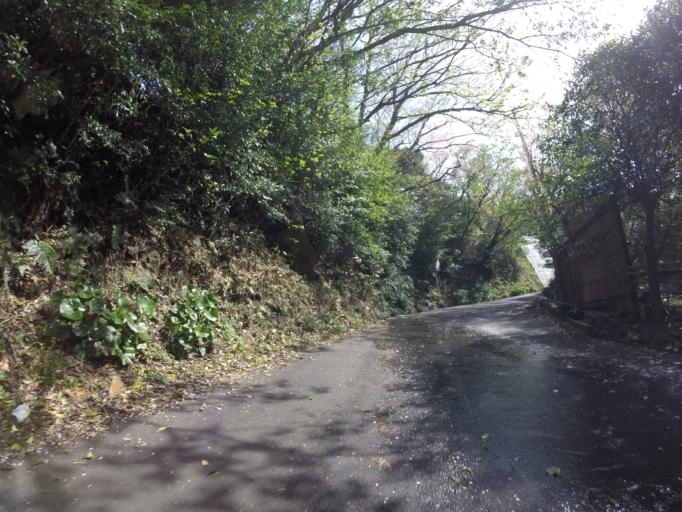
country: JP
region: Shizuoka
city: Heda
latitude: 35.0229
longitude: 138.7874
